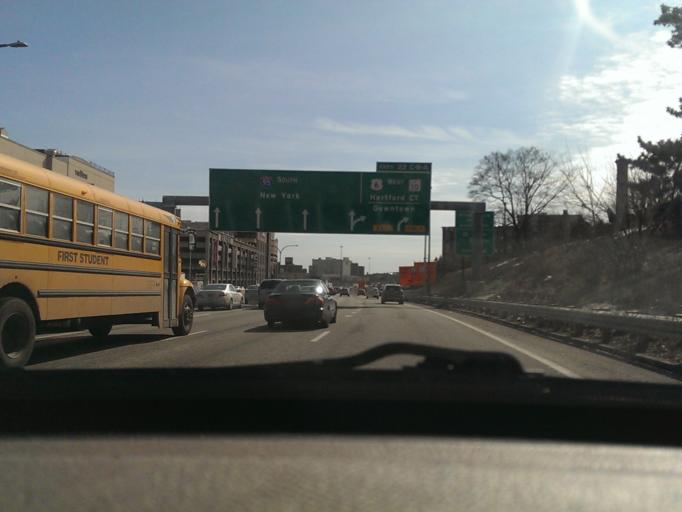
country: US
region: Rhode Island
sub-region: Providence County
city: Providence
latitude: 41.8312
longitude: -71.4178
